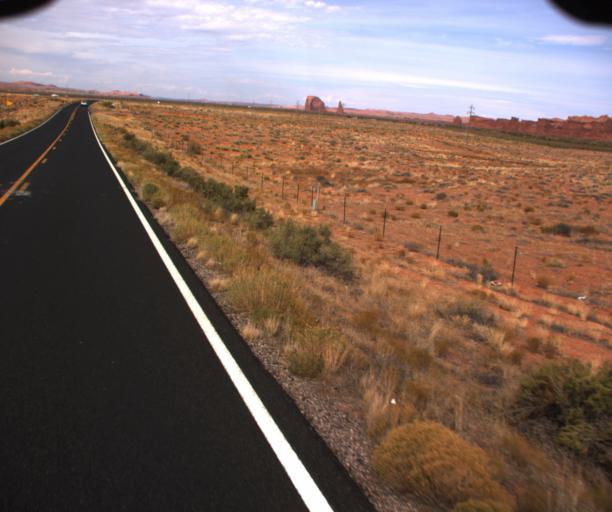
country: US
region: Arizona
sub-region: Apache County
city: Many Farms
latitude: 36.6094
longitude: -109.5759
